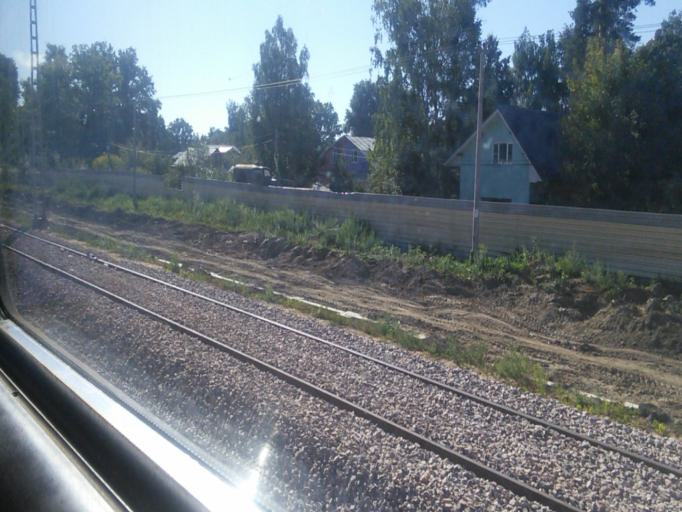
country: RU
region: Moskovskaya
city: Saltykovka
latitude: 55.7596
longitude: 37.9115
